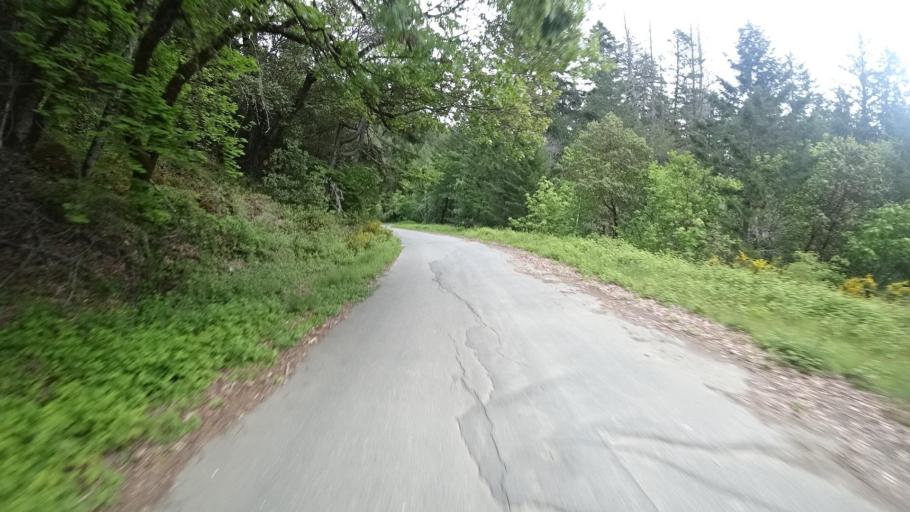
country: US
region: California
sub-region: Humboldt County
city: Willow Creek
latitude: 41.1202
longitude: -123.7397
